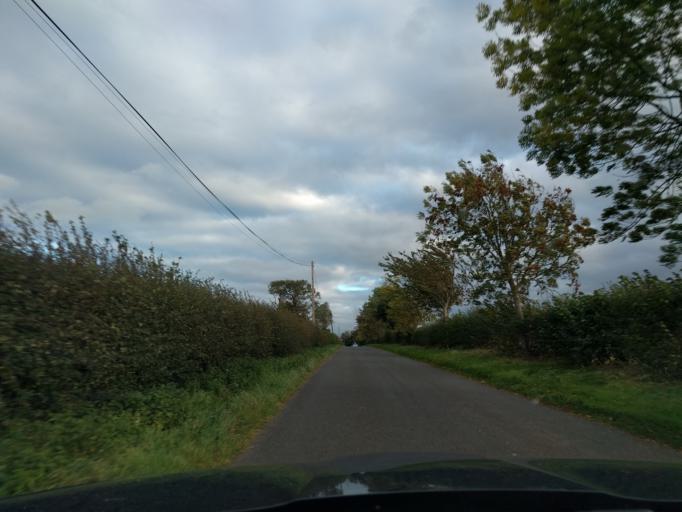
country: GB
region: England
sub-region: Northumberland
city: Ford
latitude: 55.7379
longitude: -2.1010
